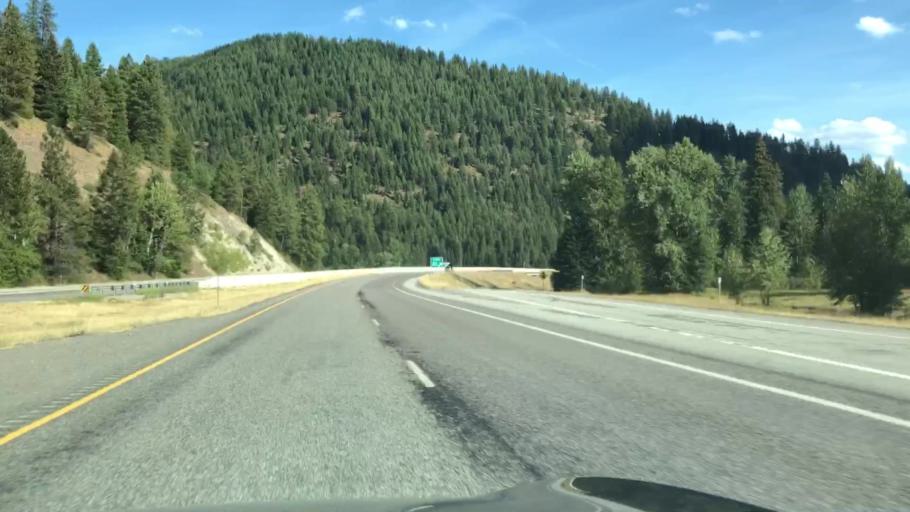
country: US
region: Montana
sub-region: Sanders County
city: Thompson Falls
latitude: 47.3560
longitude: -115.2975
